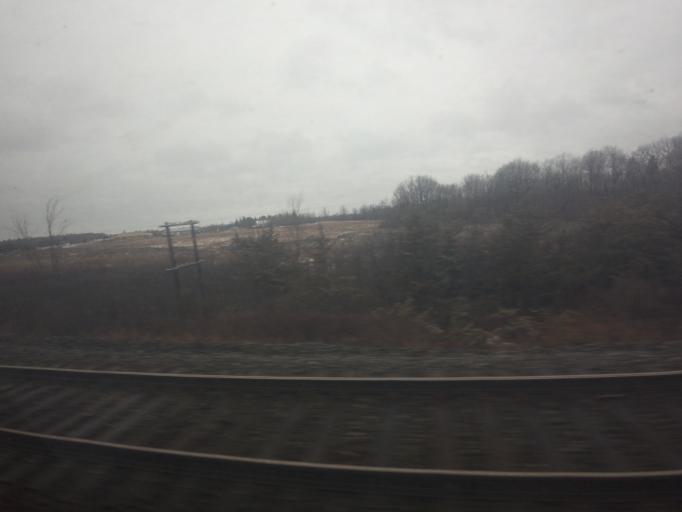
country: CA
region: Ontario
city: Kingston
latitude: 44.2324
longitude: -76.6815
